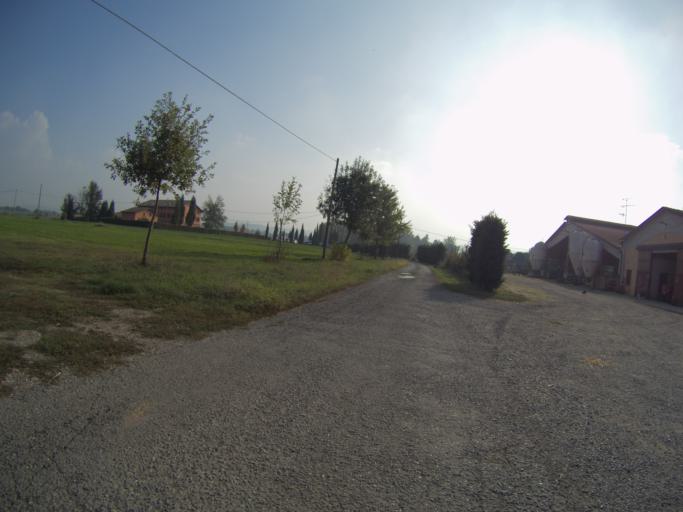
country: IT
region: Emilia-Romagna
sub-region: Provincia di Reggio Emilia
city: San Bartolomeo
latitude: 44.6528
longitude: 10.5318
